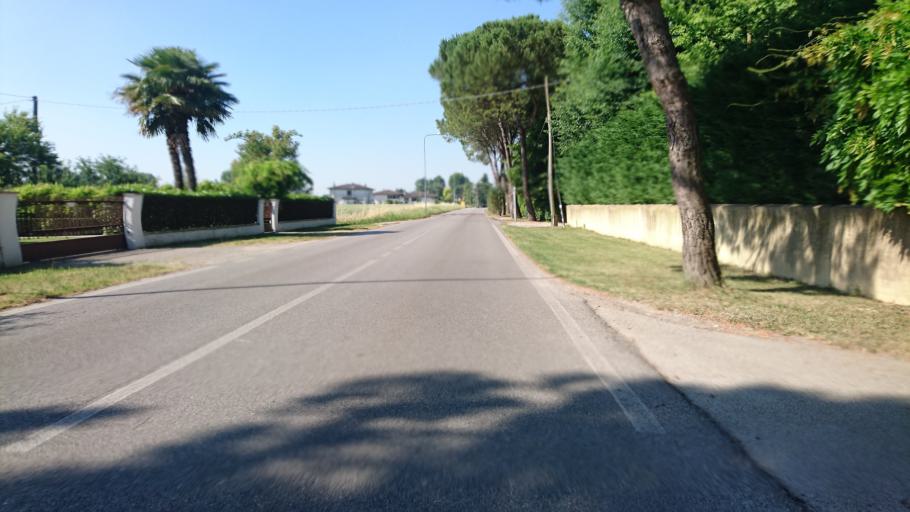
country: IT
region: Veneto
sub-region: Provincia di Padova
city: Abano Terme
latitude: 45.3644
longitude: 11.8069
